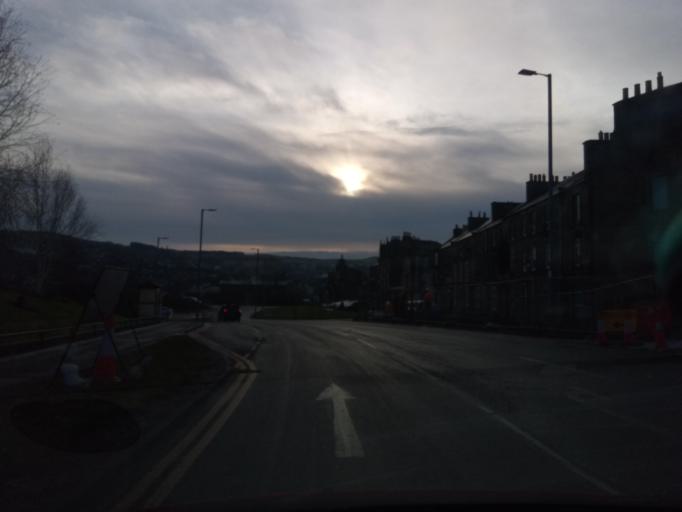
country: GB
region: Scotland
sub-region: The Scottish Borders
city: Hawick
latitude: 55.4292
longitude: -2.7853
